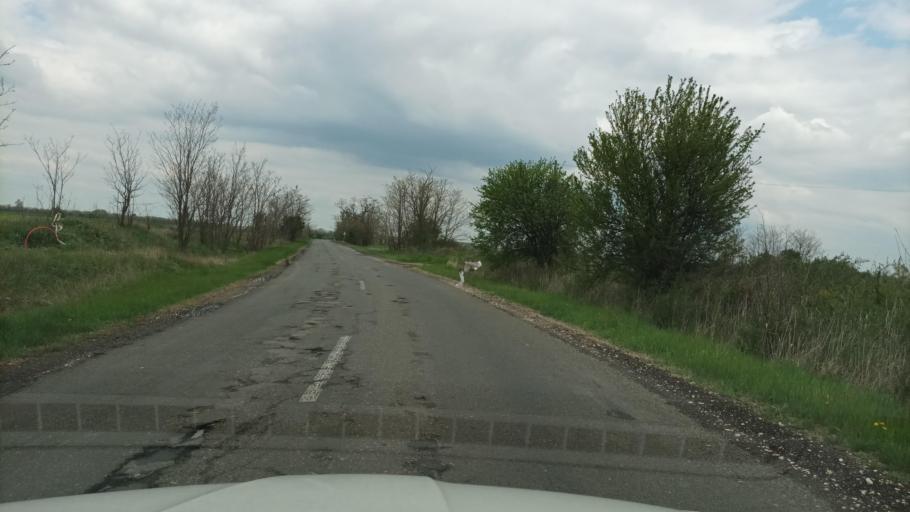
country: HU
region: Pest
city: Abony
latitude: 47.1667
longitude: 19.9782
